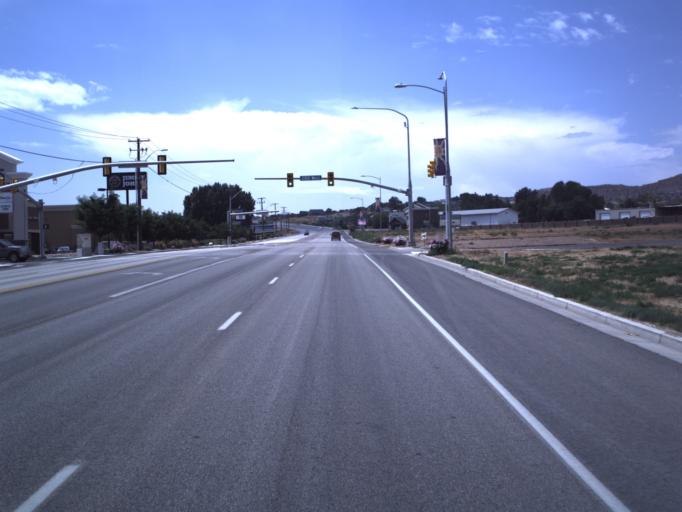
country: US
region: Utah
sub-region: Uintah County
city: Vernal
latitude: 40.4368
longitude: -109.5684
